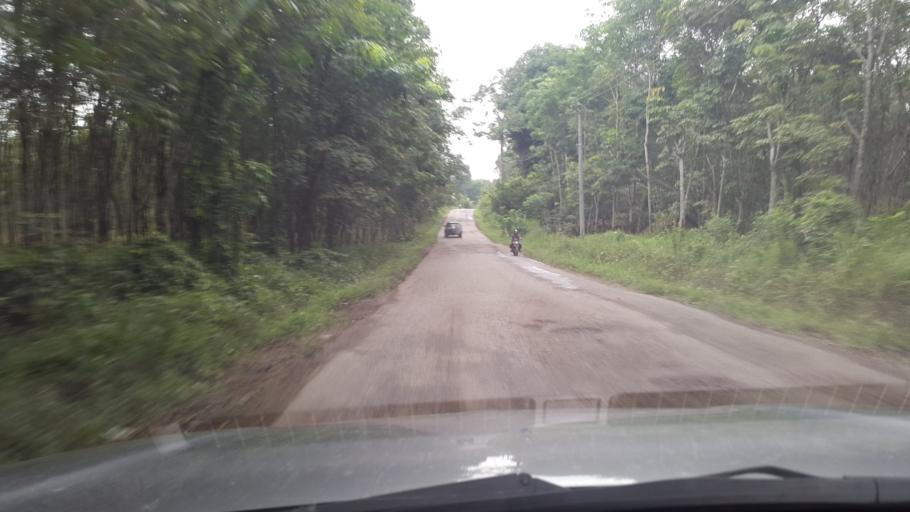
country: ID
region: South Sumatra
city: Gunungmenang
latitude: -3.3047
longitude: 104.0320
